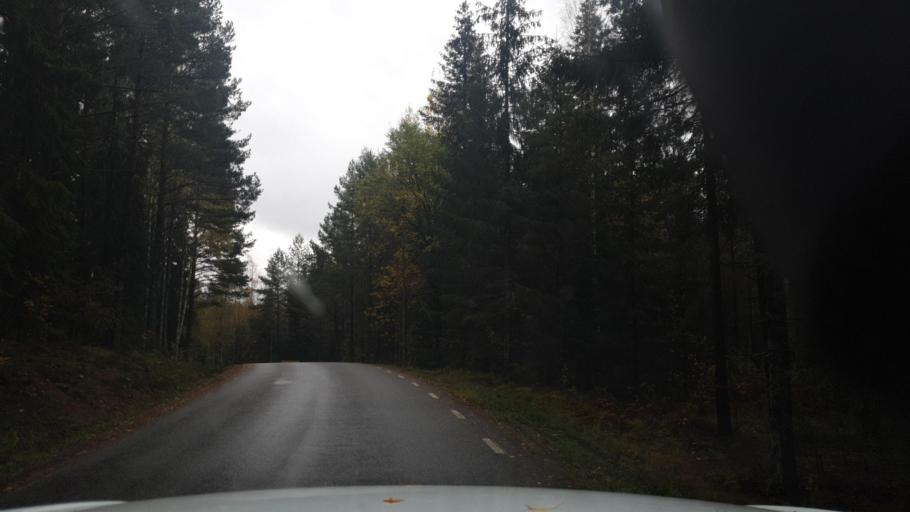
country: SE
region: Vaermland
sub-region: Karlstads Kommun
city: Valberg
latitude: 59.4161
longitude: 13.1526
